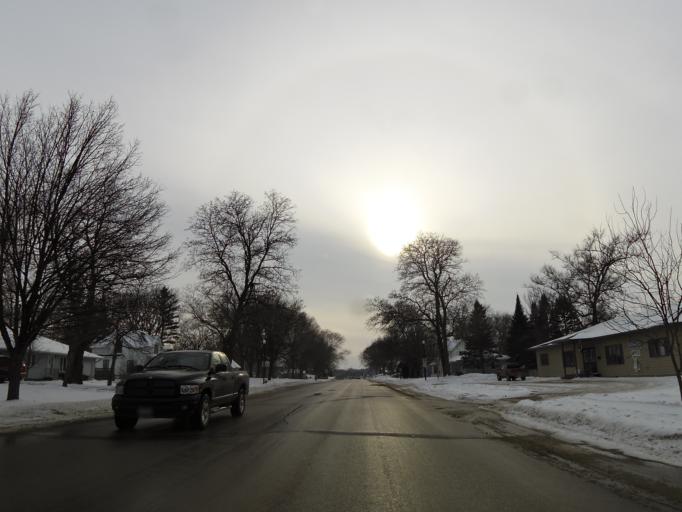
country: US
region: Minnesota
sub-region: McLeod County
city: Hutchinson
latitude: 44.8979
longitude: -94.3609
